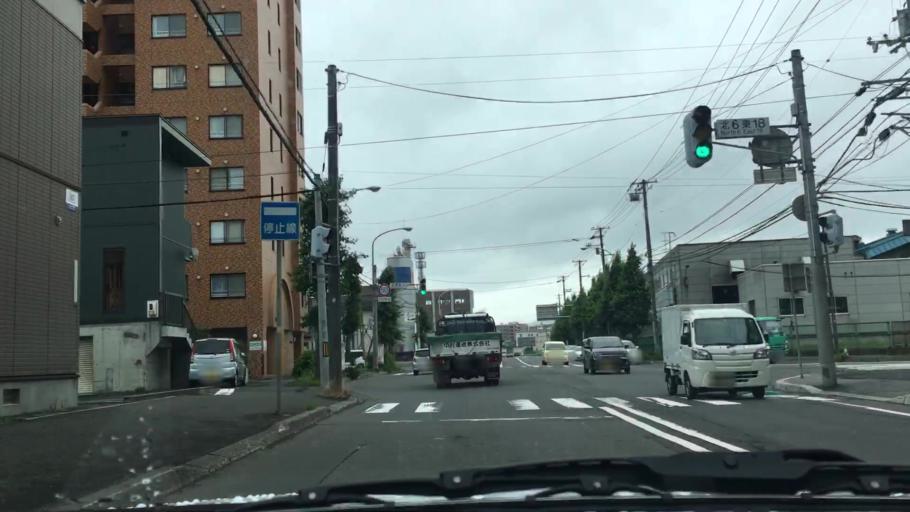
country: JP
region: Hokkaido
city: Sapporo
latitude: 43.0736
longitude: 141.3830
